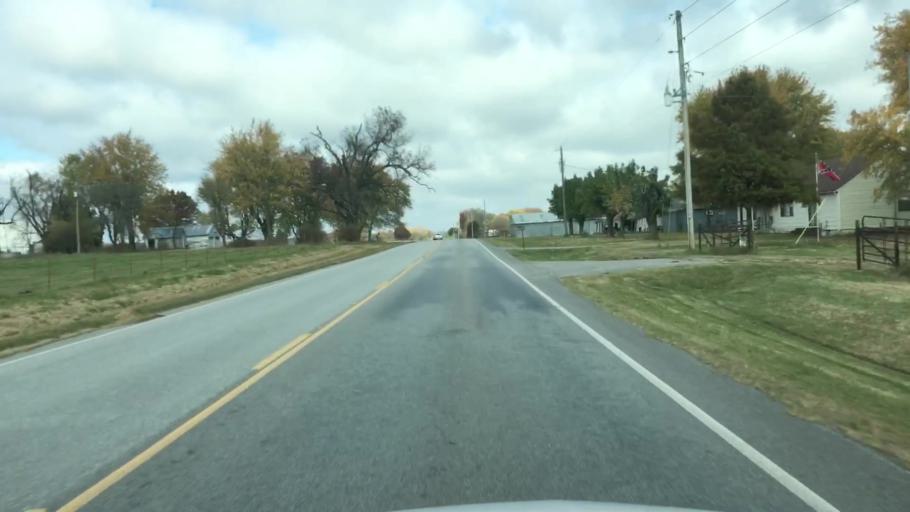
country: US
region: Arkansas
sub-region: Benton County
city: Centerton
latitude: 36.2729
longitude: -94.3502
